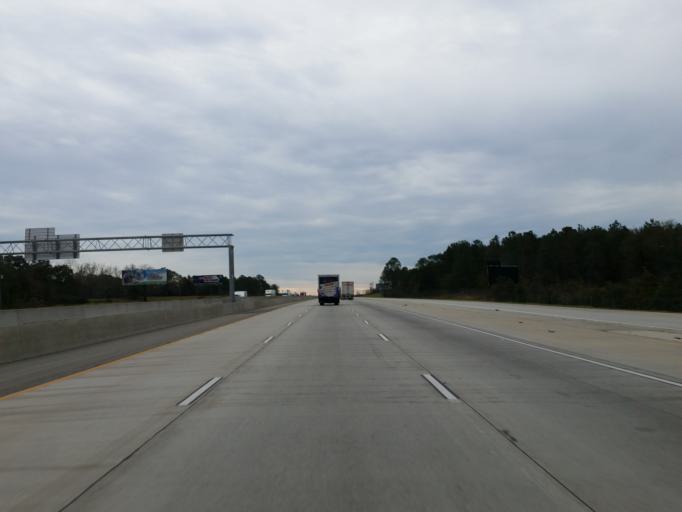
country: US
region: Georgia
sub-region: Tift County
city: Unionville
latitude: 31.3536
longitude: -83.4889
